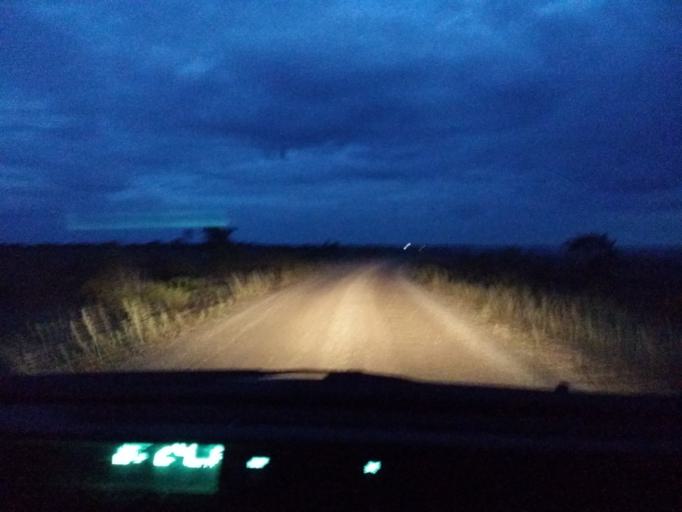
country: SE
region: Kalmar
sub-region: Borgholms Kommun
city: Borgholm
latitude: 57.1247
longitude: 16.8998
